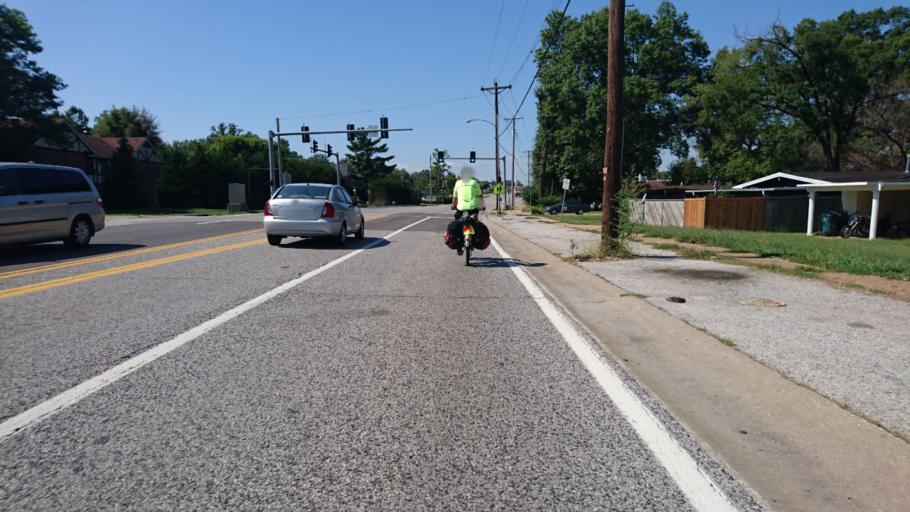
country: US
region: Missouri
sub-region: Saint Louis County
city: Des Peres
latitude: 38.5994
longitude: -90.4237
